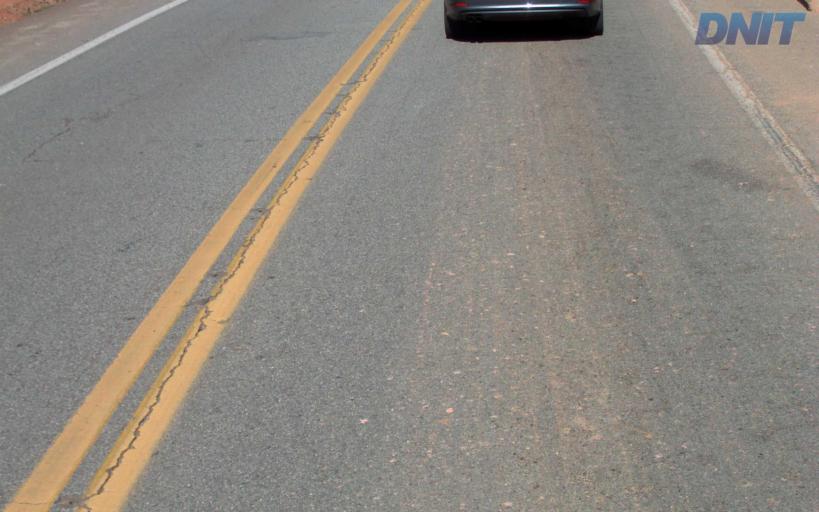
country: BR
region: Minas Gerais
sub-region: Barao De Cocais
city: Barao de Cocais
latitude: -19.7488
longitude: -43.4887
